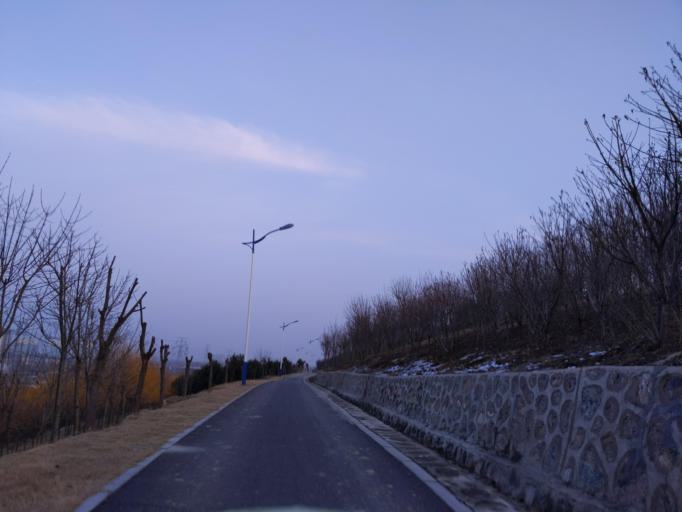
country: CN
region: Henan Sheng
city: Zhongyuanlu
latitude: 35.8171
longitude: 115.0547
